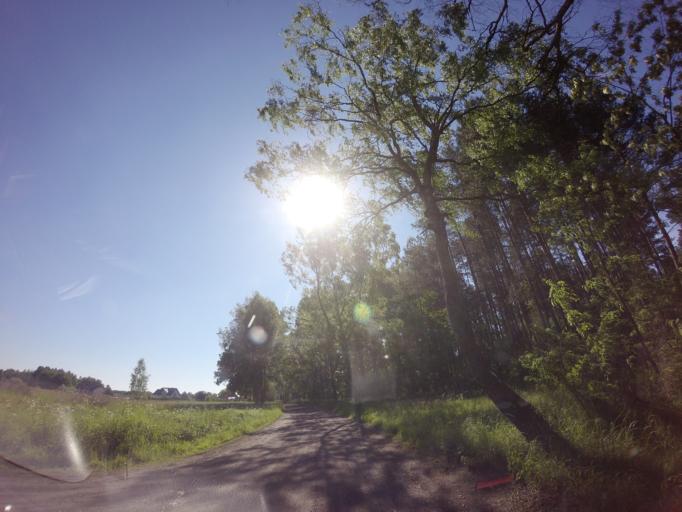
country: PL
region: West Pomeranian Voivodeship
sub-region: Powiat choszczenski
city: Drawno
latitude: 53.2140
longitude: 15.7354
